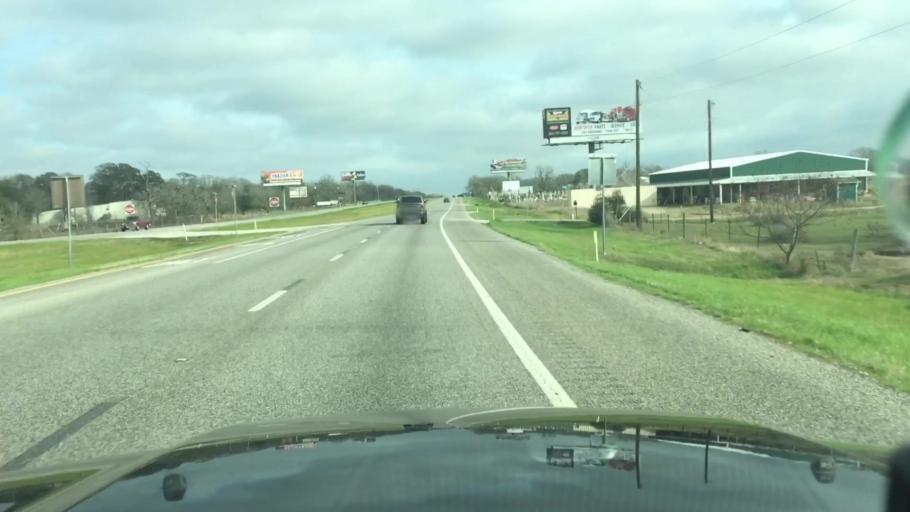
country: US
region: Texas
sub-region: Waller County
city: Hempstead
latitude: 30.1314
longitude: -96.1388
